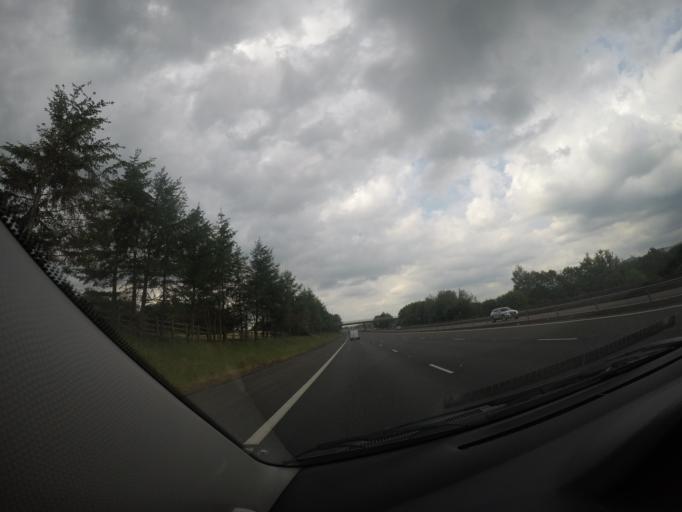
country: GB
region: Scotland
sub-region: Dumfries and Galloway
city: Moffat
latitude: 55.2764
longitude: -3.4232
